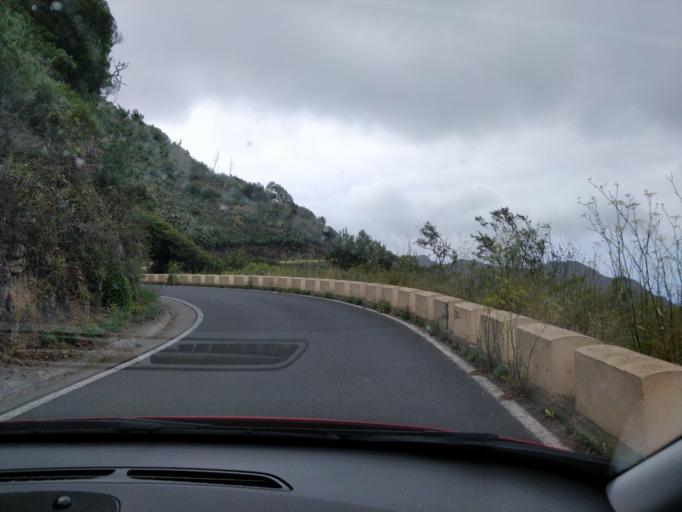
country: ES
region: Canary Islands
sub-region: Provincia de Santa Cruz de Tenerife
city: Tanque
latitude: 28.3243
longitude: -16.8521
